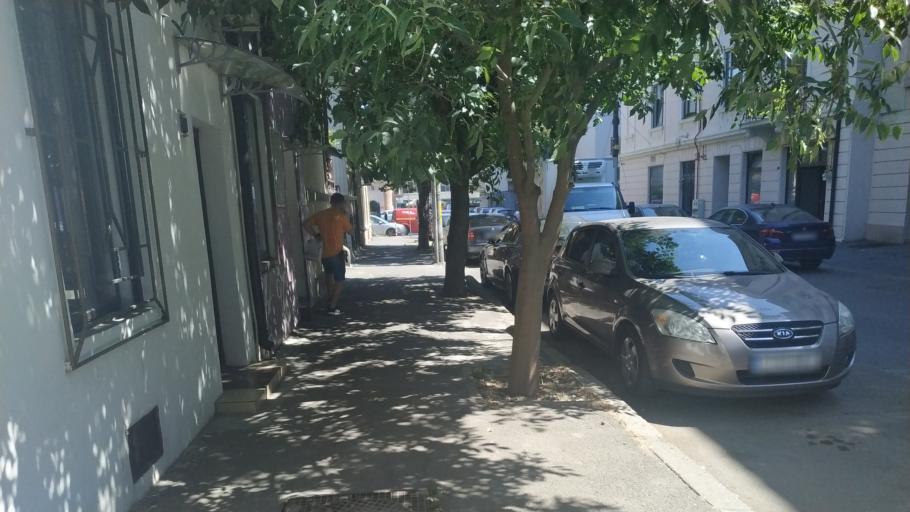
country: RO
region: Constanta
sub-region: Municipiul Constanta
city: Constanta
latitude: 44.1795
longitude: 28.6464
